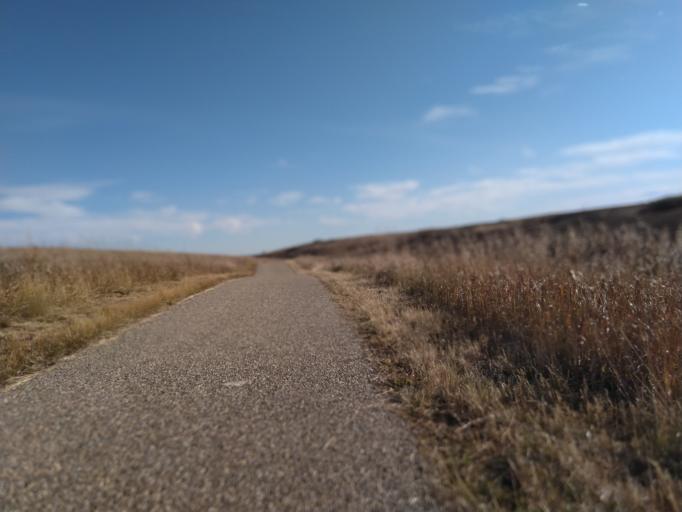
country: CA
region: Alberta
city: Calgary
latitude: 51.1208
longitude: -114.1118
